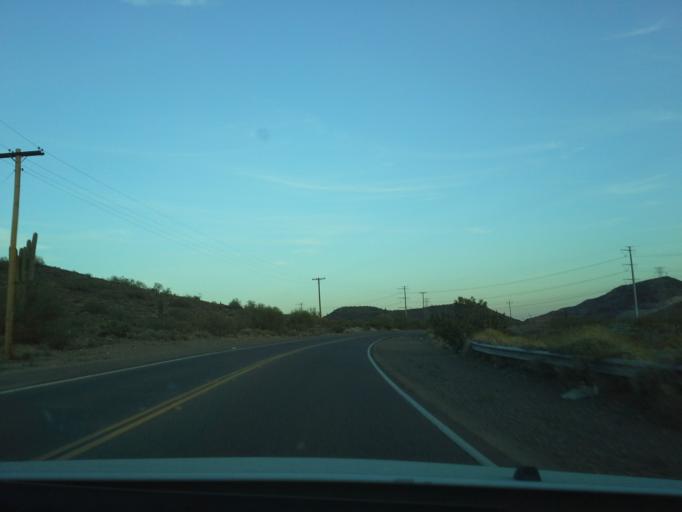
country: US
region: Arizona
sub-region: Maricopa County
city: Cave Creek
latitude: 33.7126
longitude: -112.0688
